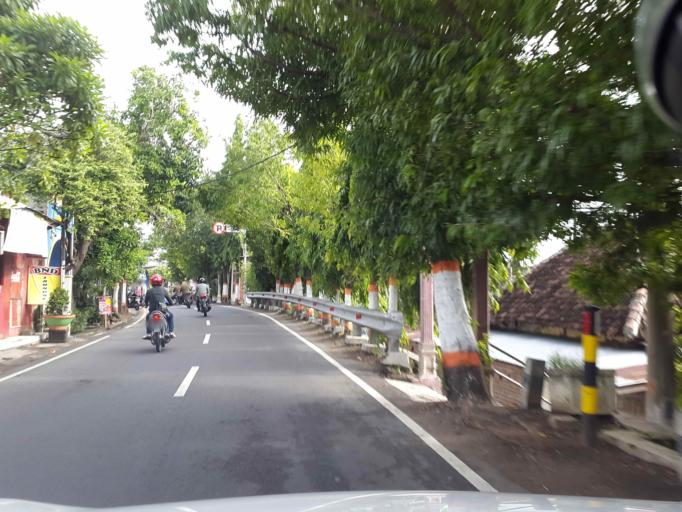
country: ID
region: East Java
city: Mojokerto
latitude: -7.4649
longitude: 112.4292
